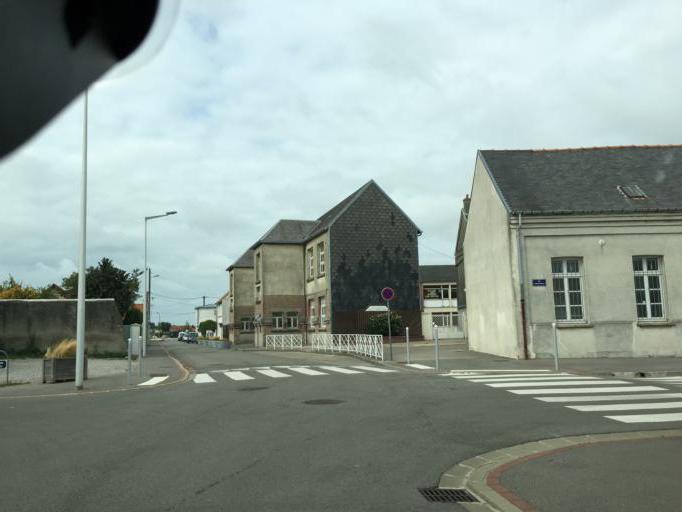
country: FR
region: Nord-Pas-de-Calais
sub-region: Departement du Pas-de-Calais
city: Berck
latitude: 50.4094
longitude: 1.5921
